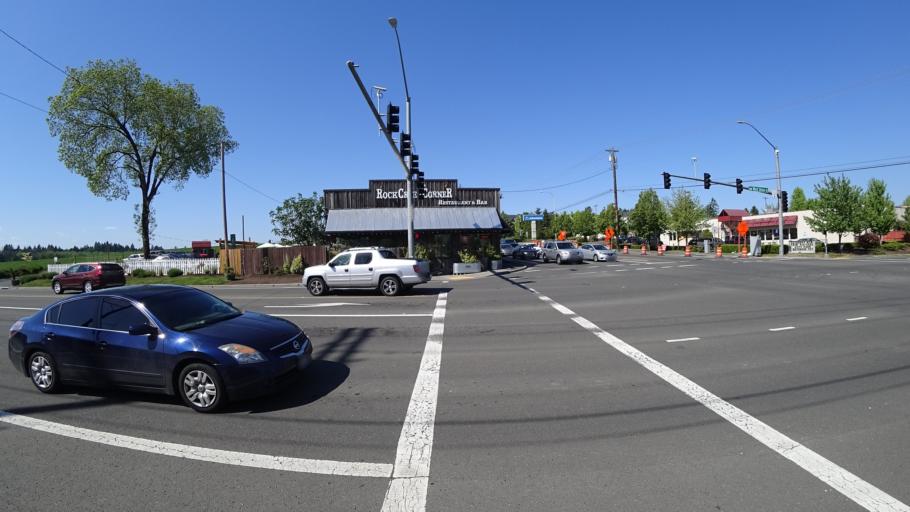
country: US
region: Oregon
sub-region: Washington County
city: Bethany
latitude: 45.5580
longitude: -122.8679
